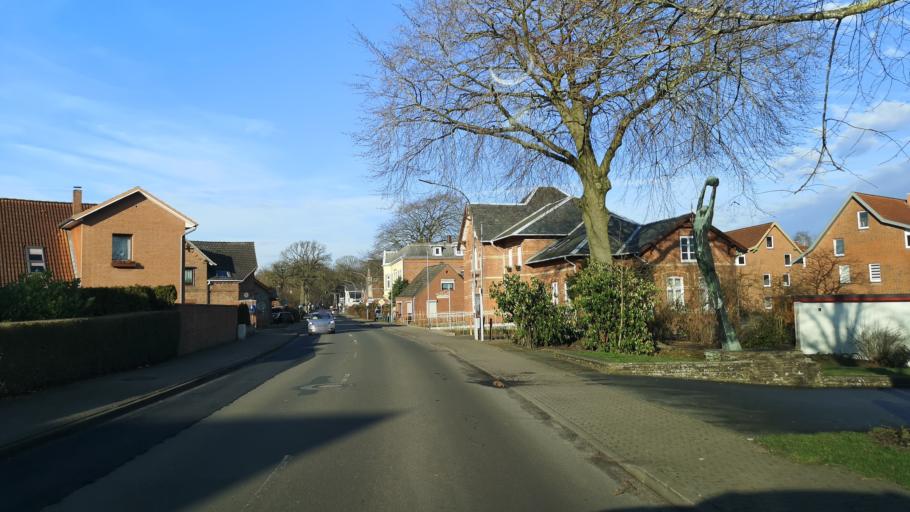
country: DE
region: Schleswig-Holstein
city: Lagerdorf
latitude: 53.8878
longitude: 9.5770
